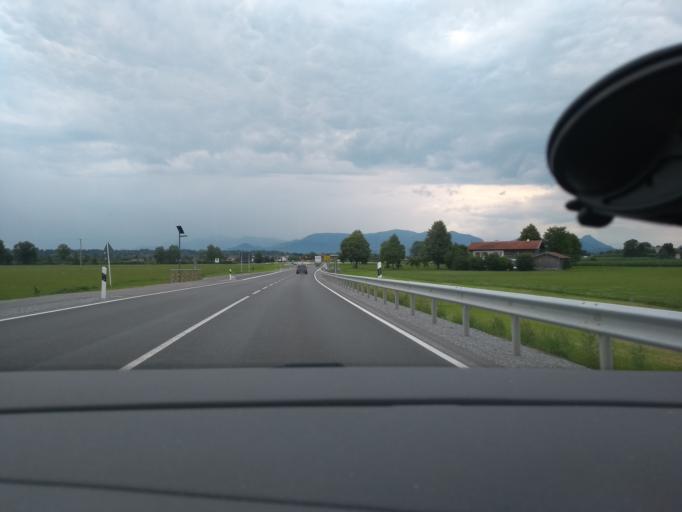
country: DE
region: Bavaria
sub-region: Upper Bavaria
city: Grosskarolinenfeld
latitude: 47.8865
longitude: 12.1121
